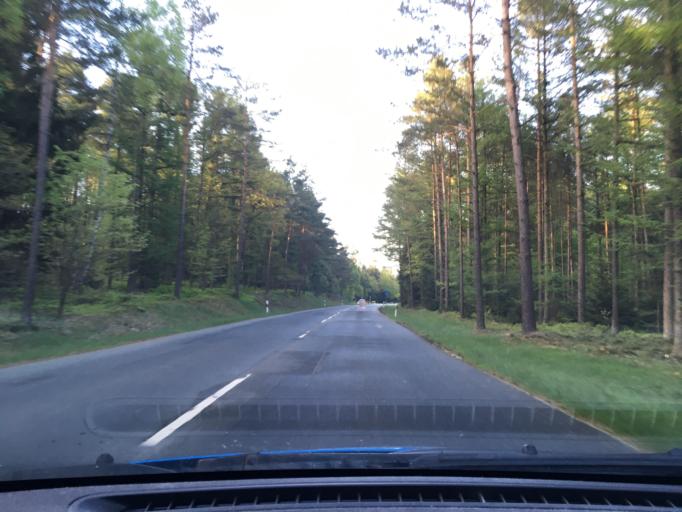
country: DE
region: Lower Saxony
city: Wietzendorf
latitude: 52.9948
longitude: 9.9953
